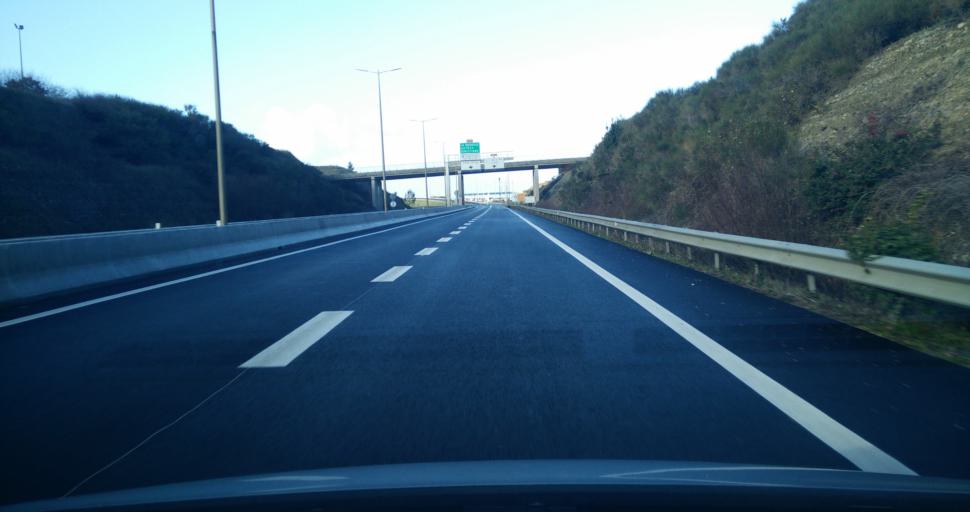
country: FR
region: Poitou-Charentes
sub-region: Departement de la Charente-Maritime
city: Nieul-sur-Mer
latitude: 46.1754
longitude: -1.2096
